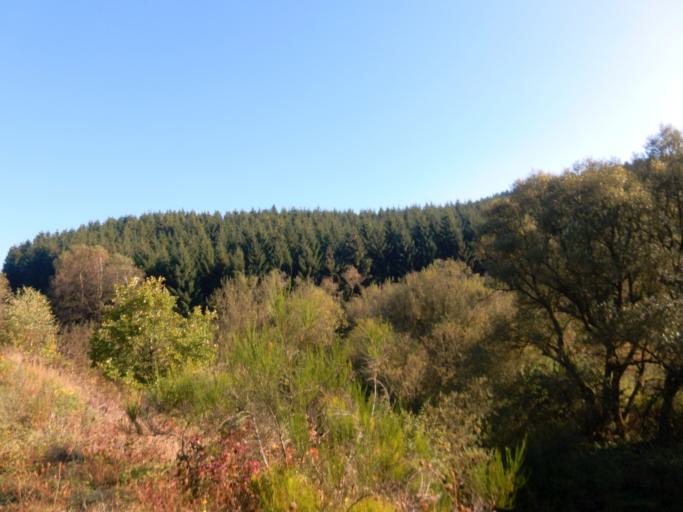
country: LU
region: Diekirch
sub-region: Canton de Clervaux
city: Troisvierges
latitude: 50.1262
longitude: 5.9872
